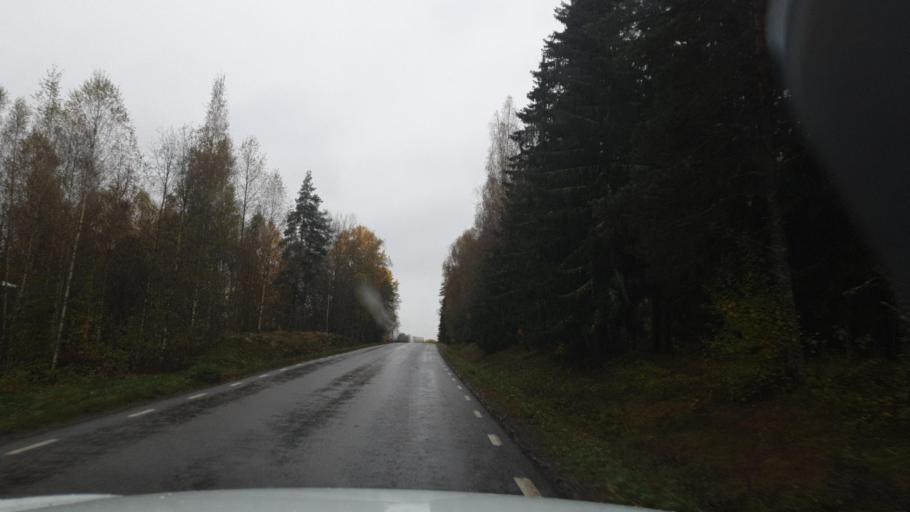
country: SE
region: Vaermland
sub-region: Eda Kommun
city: Charlottenberg
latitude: 59.7995
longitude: 12.1542
